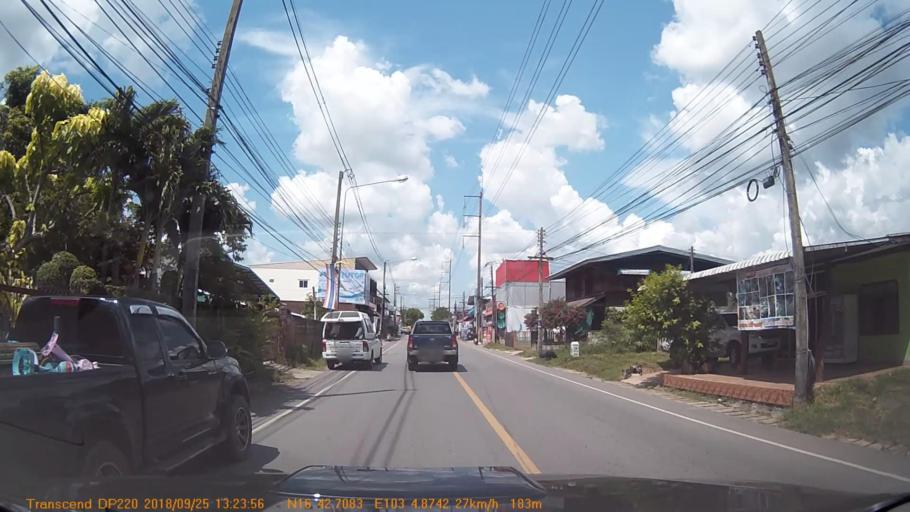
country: TH
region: Khon Kaen
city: Kranuan
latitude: 16.7119
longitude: 103.0813
